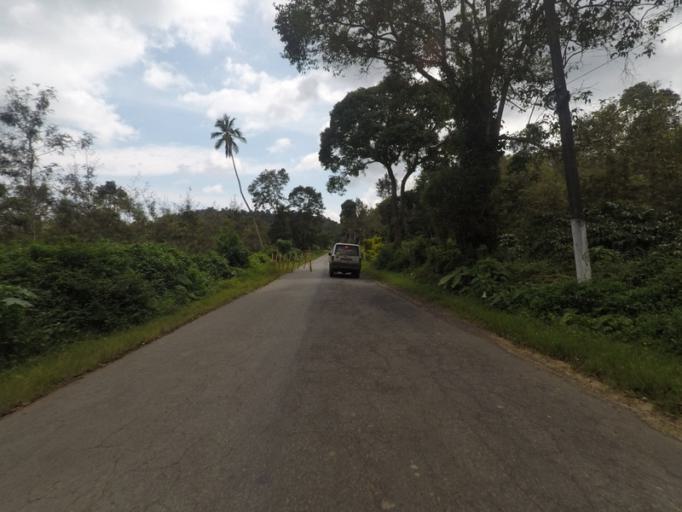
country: IN
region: Karnataka
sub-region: Kodagu
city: Virarajendrapet
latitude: 12.2533
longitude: 75.8685
